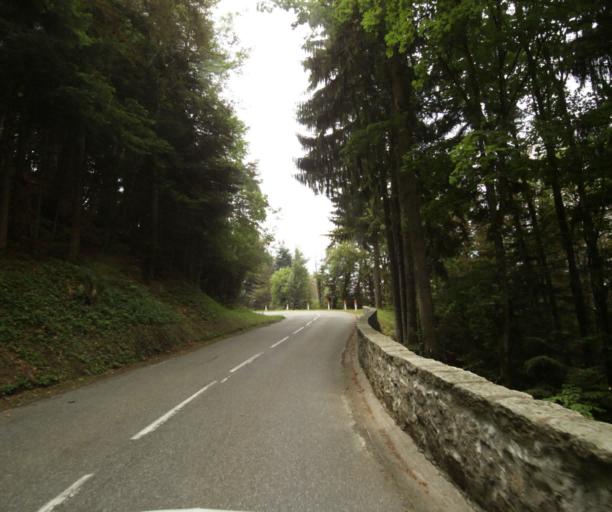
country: FR
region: Rhone-Alpes
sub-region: Departement de la Haute-Savoie
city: Perrignier
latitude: 46.2771
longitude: 6.4559
